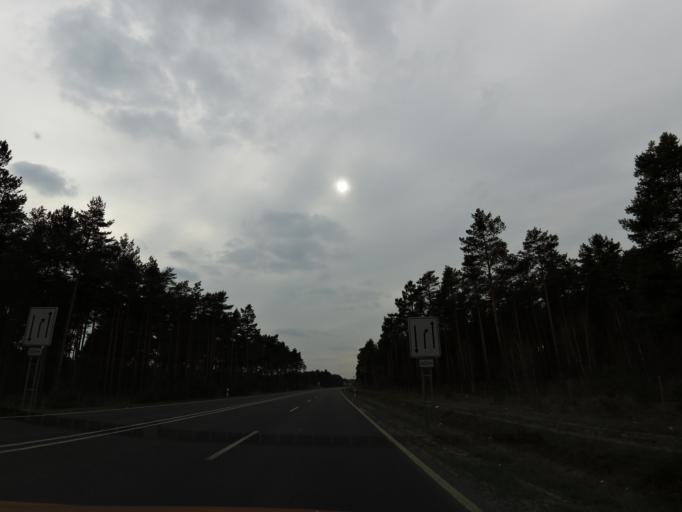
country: DE
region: Brandenburg
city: Mullrose
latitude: 52.2677
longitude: 14.4316
